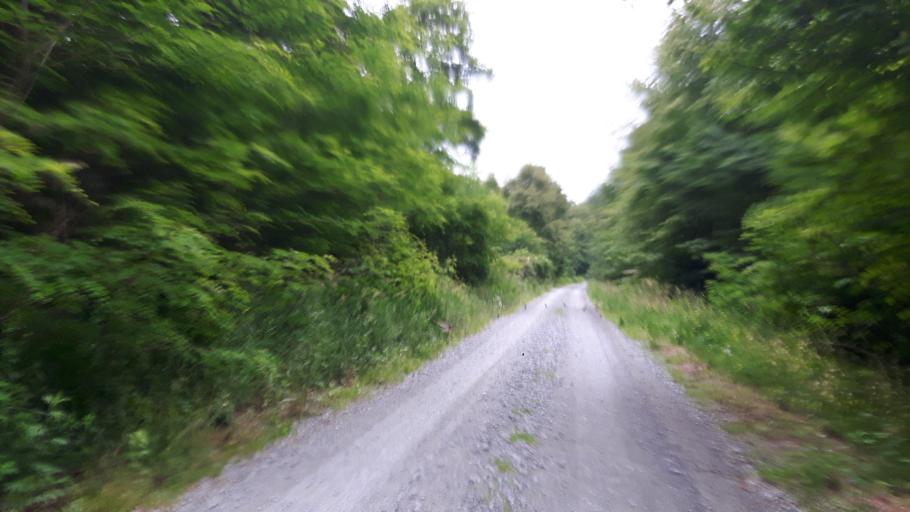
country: PL
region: Warmian-Masurian Voivodeship
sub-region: Powiat elblaski
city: Tolkmicko
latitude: 54.3359
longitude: 19.5647
